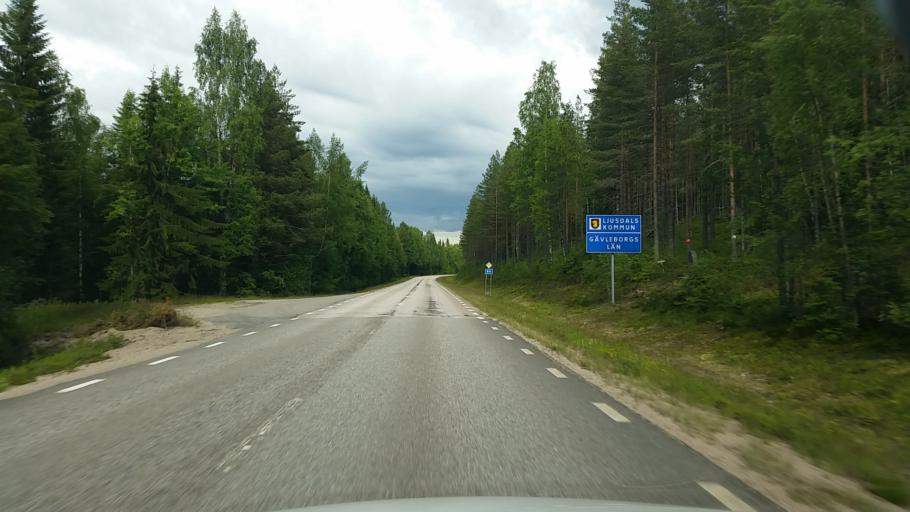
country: SE
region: Jaemtland
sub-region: Harjedalens Kommun
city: Sveg
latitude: 61.9796
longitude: 15.1008
